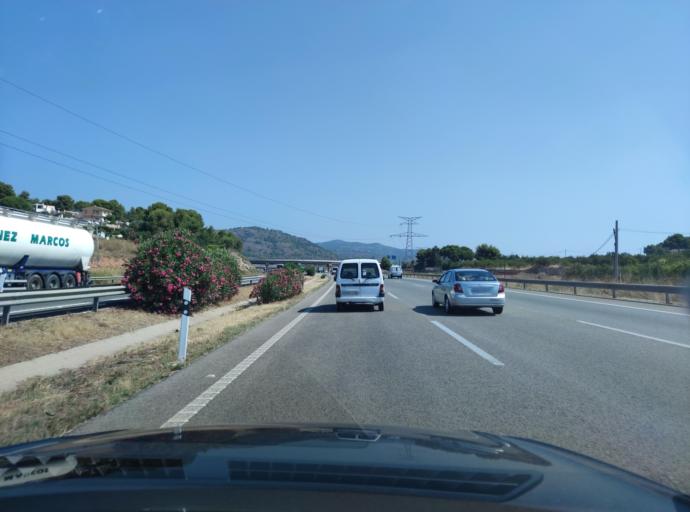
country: ES
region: Valencia
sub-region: Provincia de Valencia
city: Petres
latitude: 39.6679
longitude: -0.3020
